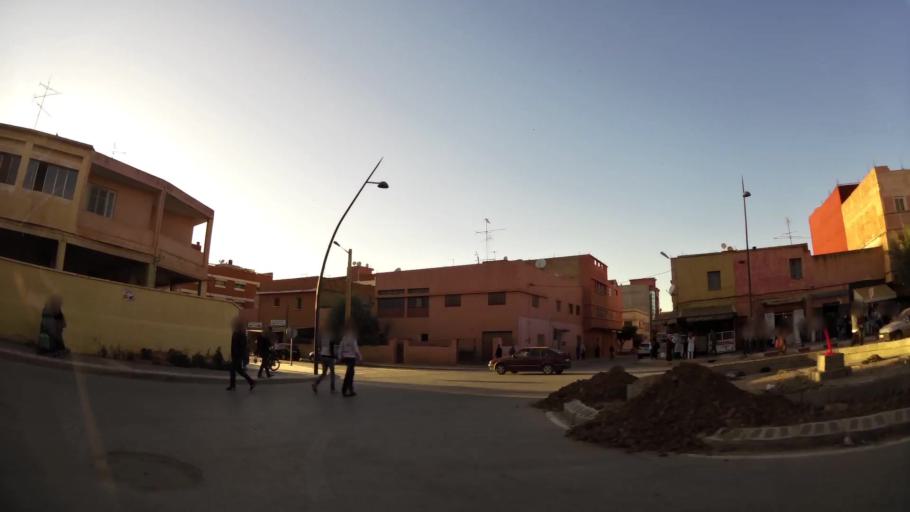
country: MA
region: Oriental
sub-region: Berkane-Taourirt
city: Berkane
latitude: 34.9205
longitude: -2.3247
